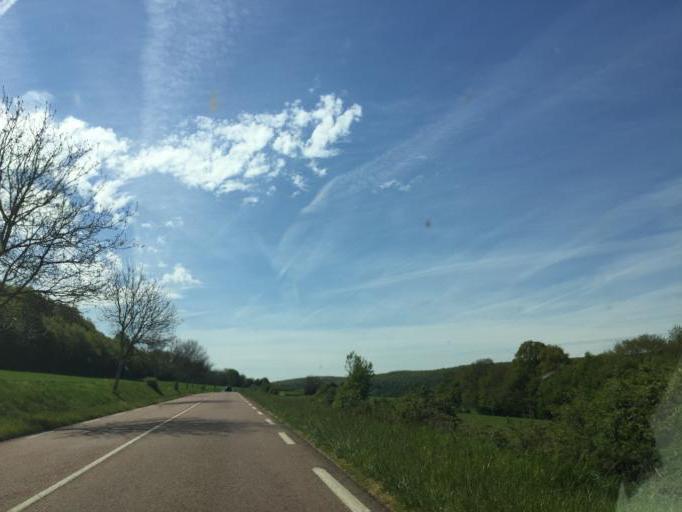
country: FR
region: Bourgogne
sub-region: Departement de la Nievre
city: Clamecy
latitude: 47.4422
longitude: 3.5584
